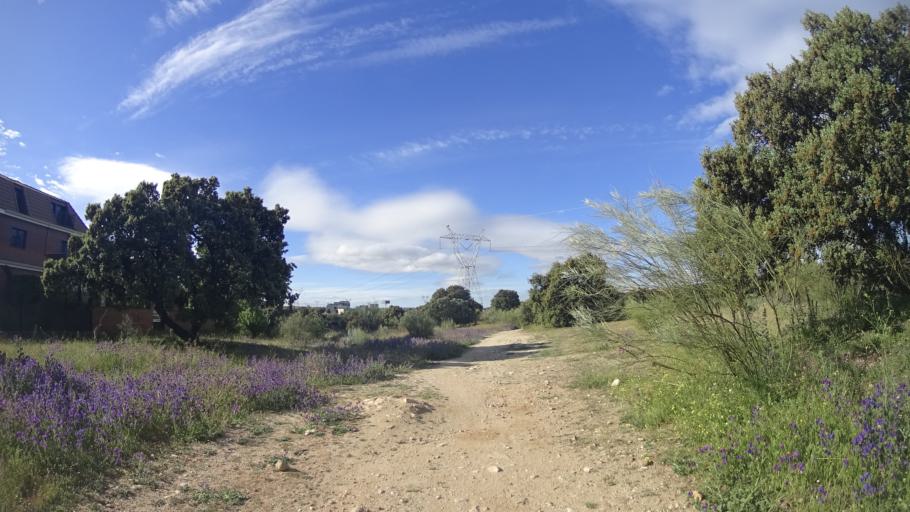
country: ES
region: Madrid
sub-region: Provincia de Madrid
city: Villanueva del Pardillo
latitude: 40.5241
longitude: -3.9357
